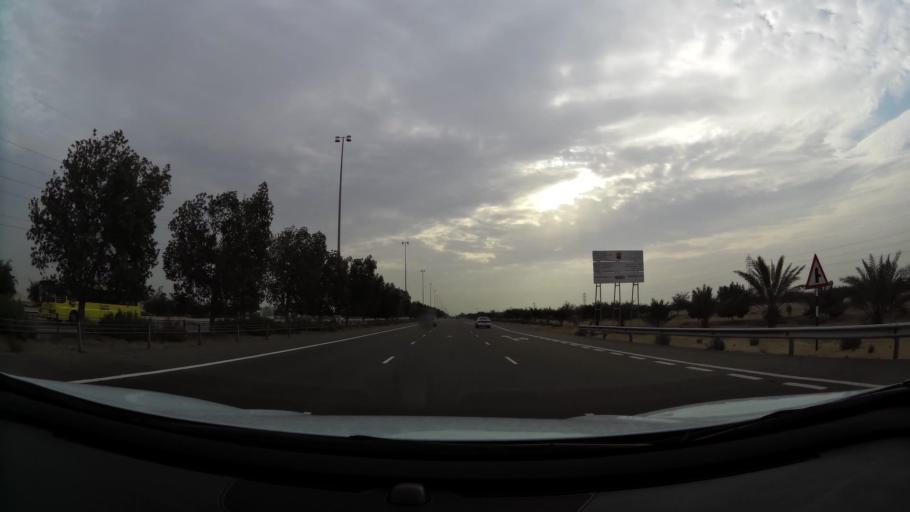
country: AE
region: Abu Dhabi
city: Abu Dhabi
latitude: 24.2207
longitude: 54.8323
